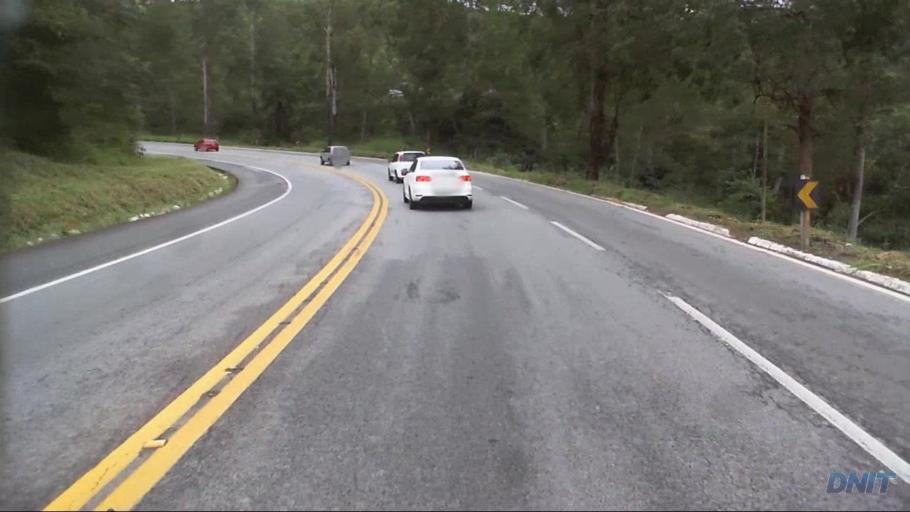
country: BR
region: Minas Gerais
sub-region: Joao Monlevade
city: Joao Monlevade
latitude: -19.8505
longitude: -43.2678
